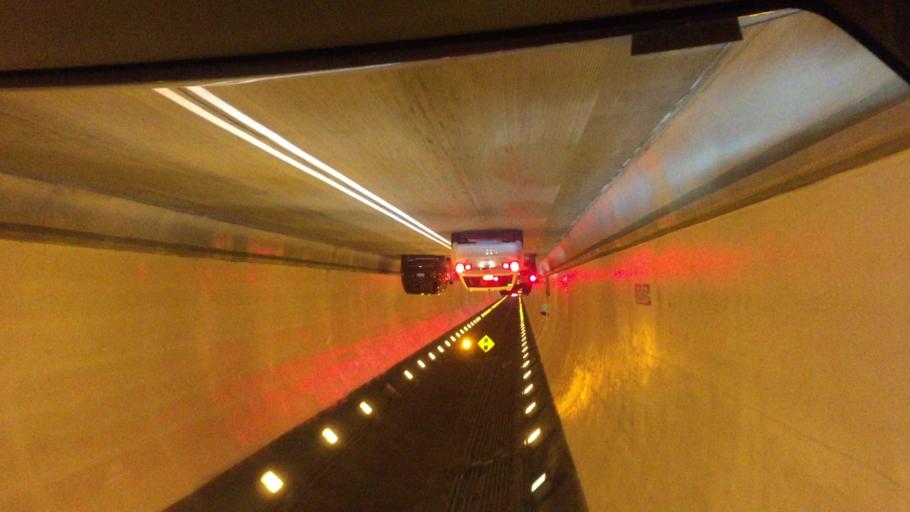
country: US
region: Pennsylvania
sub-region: Allegheny County
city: Mount Oliver
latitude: 40.4217
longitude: -80.0052
